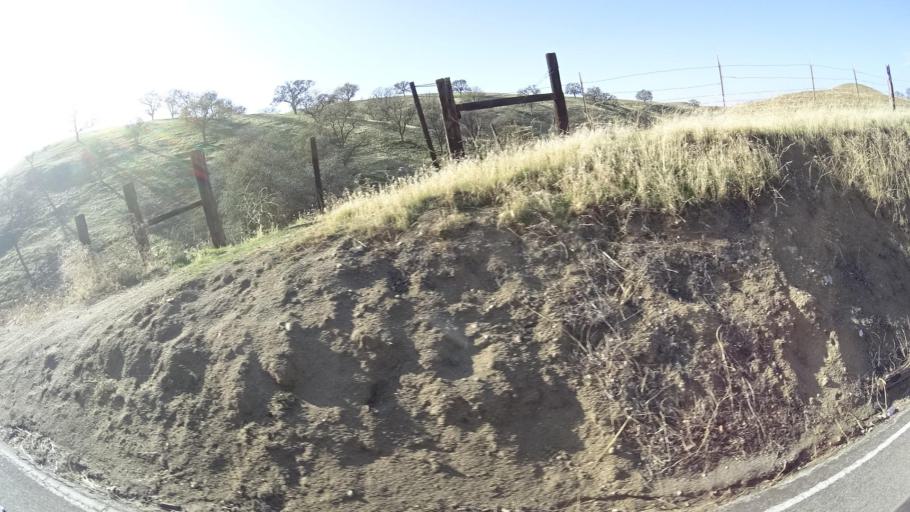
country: US
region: California
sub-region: Kern County
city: Bear Valley Springs
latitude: 35.2783
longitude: -118.6241
